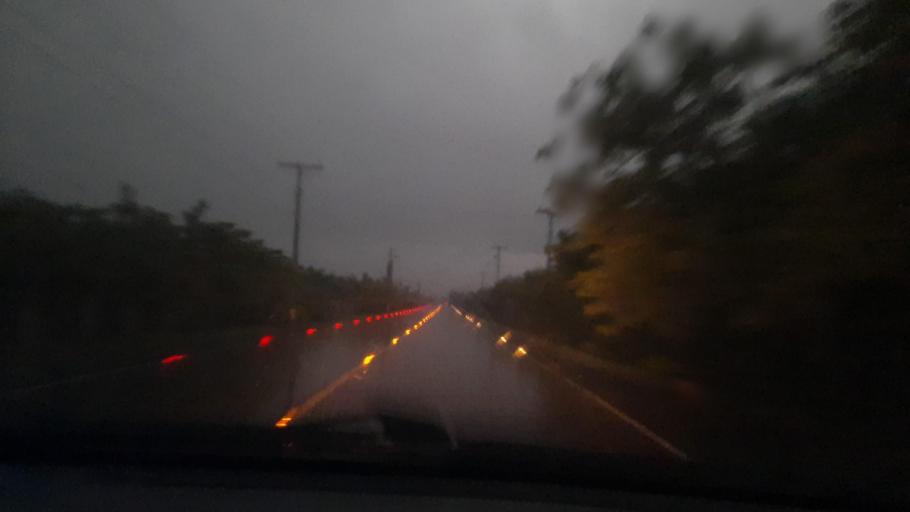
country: HN
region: Cortes
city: Potrerillos
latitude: 15.6397
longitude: -88.4187
